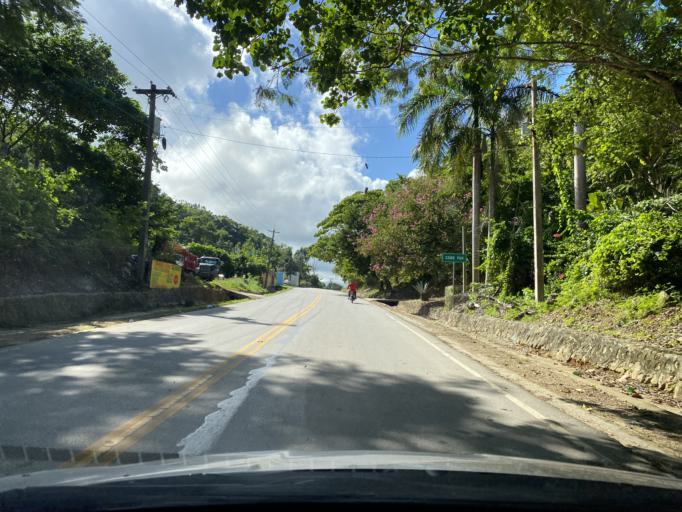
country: DO
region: Samana
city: Las Terrenas
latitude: 19.3103
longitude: -69.5331
